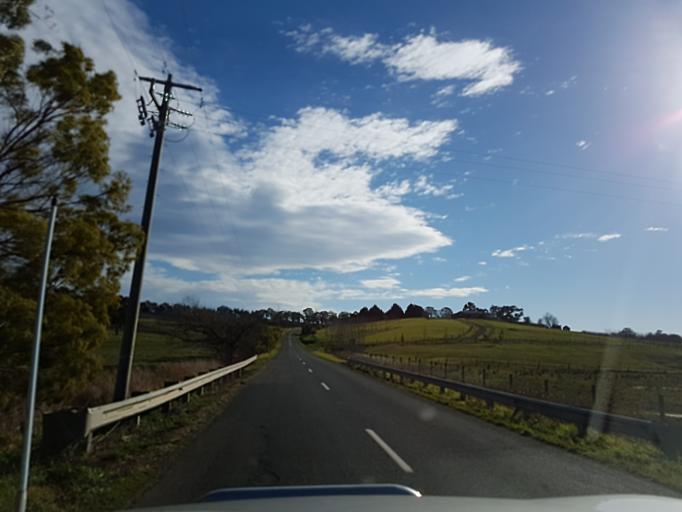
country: AU
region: Victoria
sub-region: Yarra Ranges
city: Healesville
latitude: -37.6594
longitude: 145.4614
